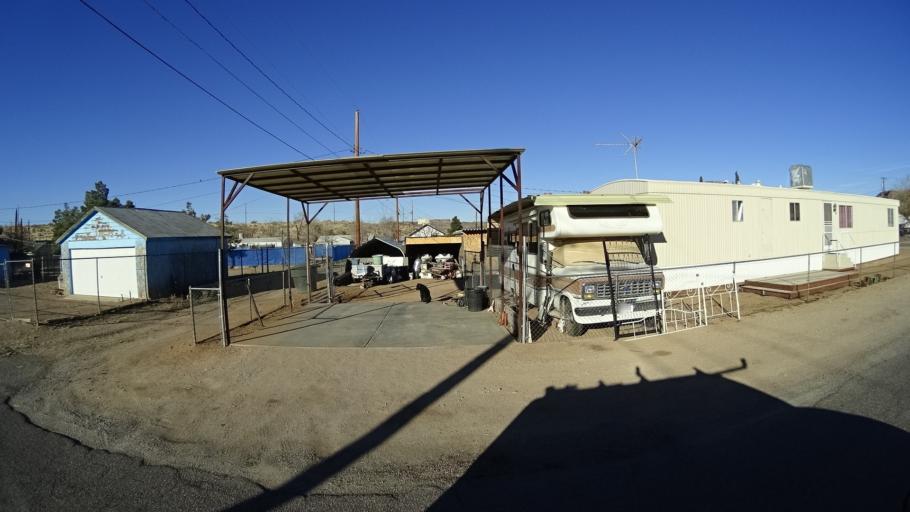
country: US
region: Arizona
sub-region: Mohave County
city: Kingman
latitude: 35.1842
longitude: -114.0431
